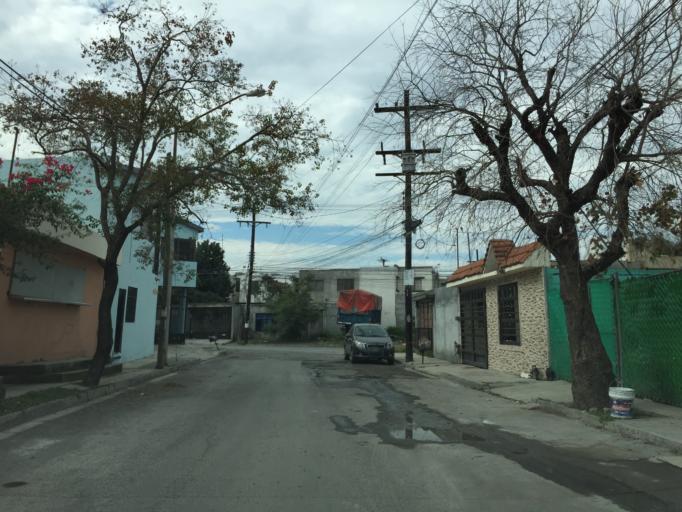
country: MX
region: Nuevo Leon
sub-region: Juarez
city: Jardines de la Silla (Jardines)
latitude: 25.6507
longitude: -100.1886
